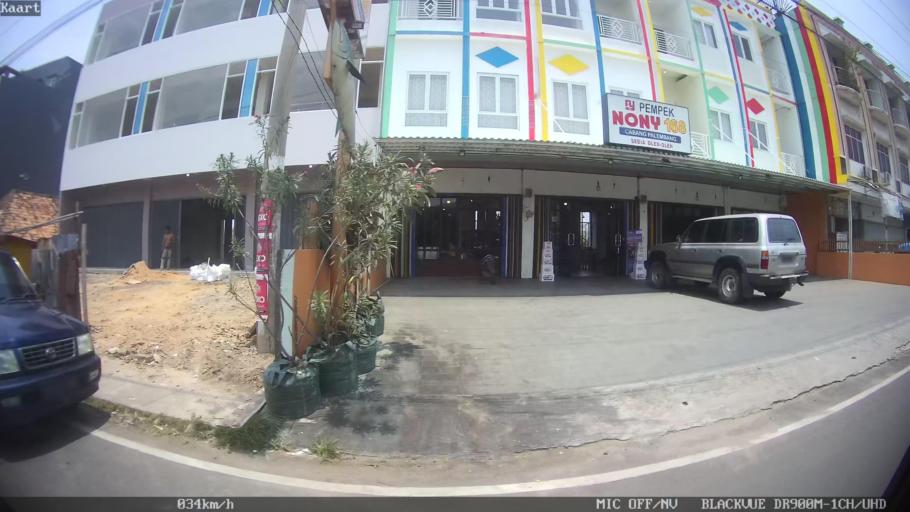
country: ID
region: Lampung
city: Bandarlampung
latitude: -5.4415
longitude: 105.2716
